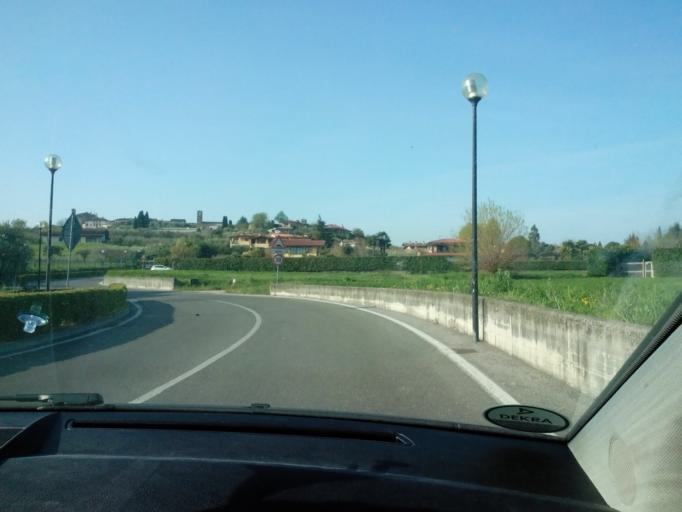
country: IT
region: Lombardy
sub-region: Provincia di Brescia
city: Solarolo
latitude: 45.5559
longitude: 10.5534
